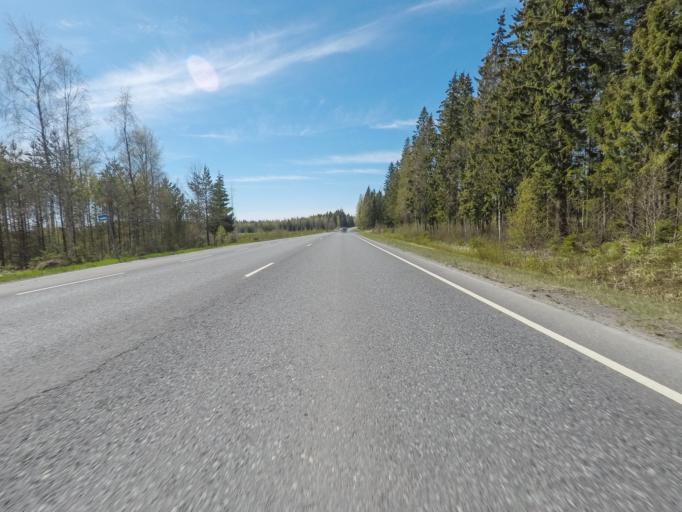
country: FI
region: Haeme
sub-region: Forssa
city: Humppila
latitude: 60.9666
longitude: 23.3937
